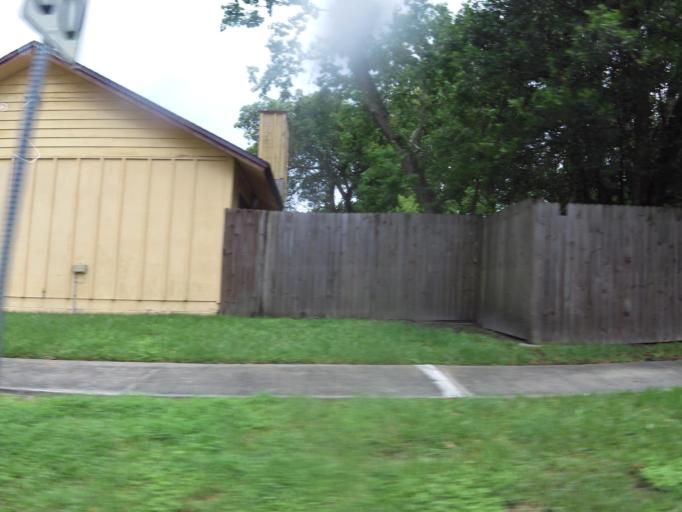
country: US
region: Florida
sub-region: Duval County
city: Jacksonville
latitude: 30.4279
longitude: -81.7013
